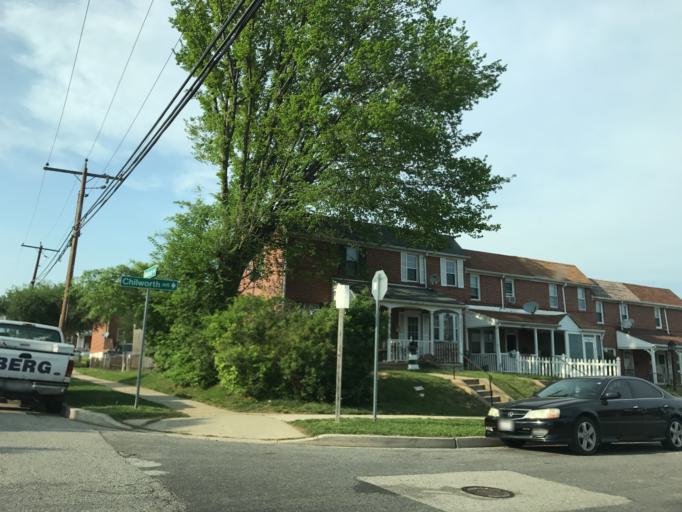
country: US
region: Maryland
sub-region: Baltimore County
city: Middle River
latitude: 39.3364
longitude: -76.4445
